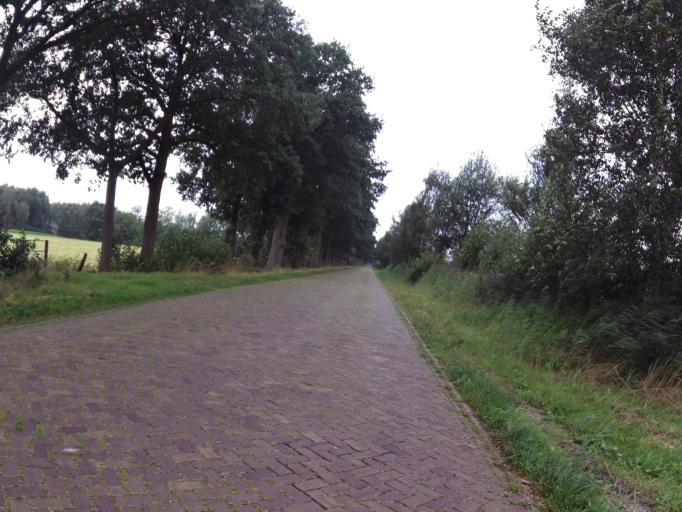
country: NL
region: Drenthe
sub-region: Gemeente Emmen
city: Schoonebeek
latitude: 52.6828
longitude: 6.9312
